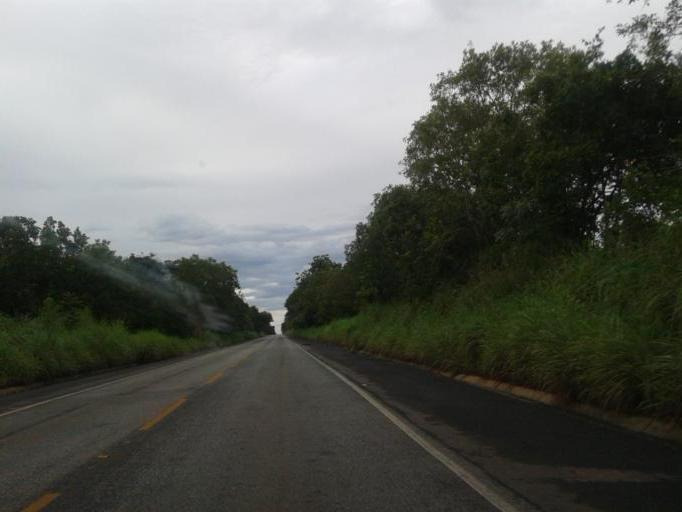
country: BR
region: Goias
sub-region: Mozarlandia
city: Mozarlandia
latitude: -14.8190
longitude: -50.5310
